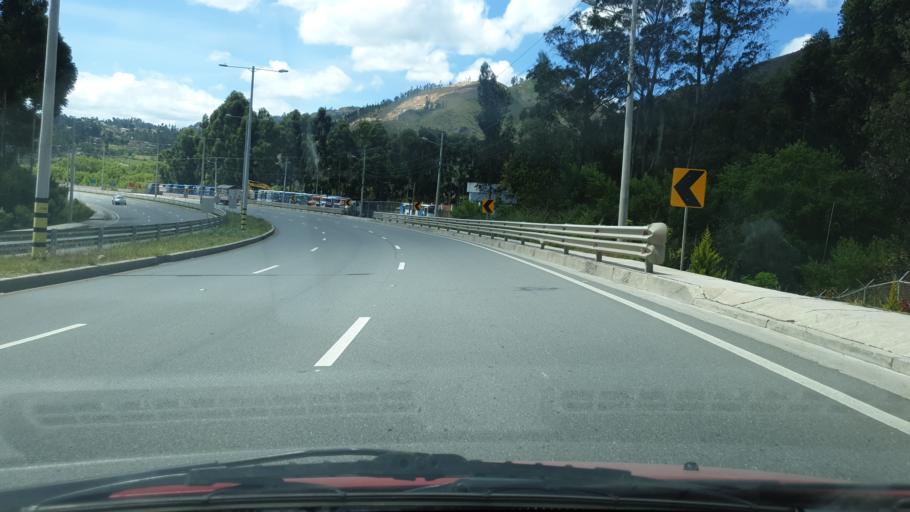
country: EC
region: Azuay
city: Llacao
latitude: -2.8438
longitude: -78.8786
